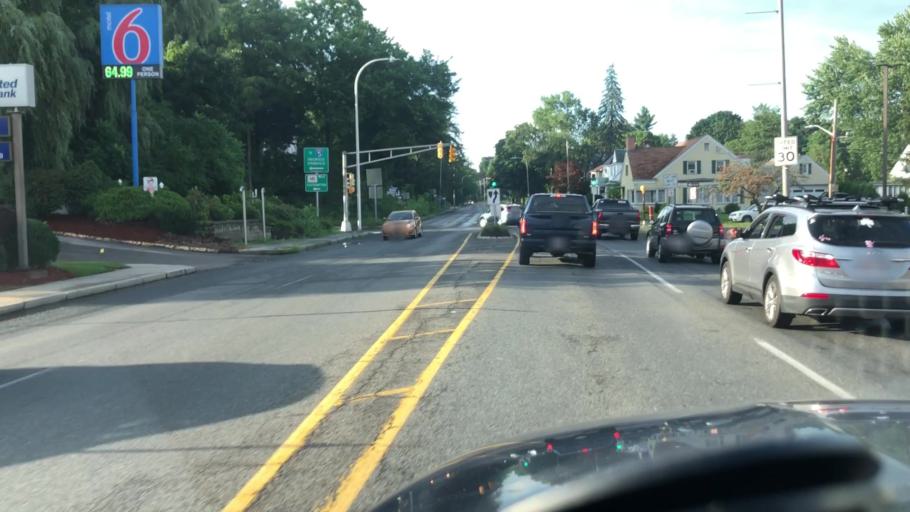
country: US
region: Massachusetts
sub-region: Hampden County
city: Holyoke
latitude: 42.2124
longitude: -72.6296
